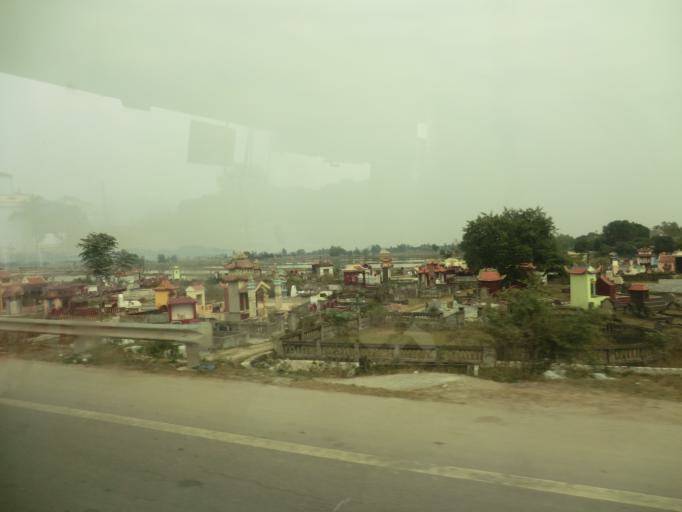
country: VN
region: Ha Nam
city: Thi Tran Thanh Luu
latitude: 20.3983
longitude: 105.9190
